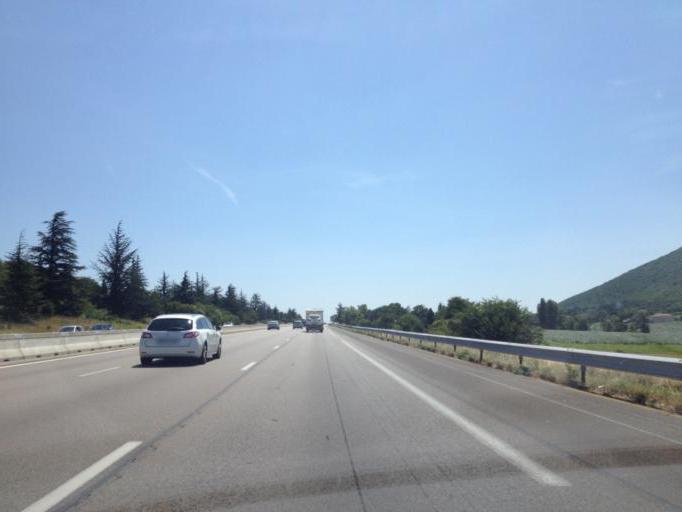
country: FR
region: Rhone-Alpes
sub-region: Departement de la Drome
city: Savasse
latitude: 44.6309
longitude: 4.7924
